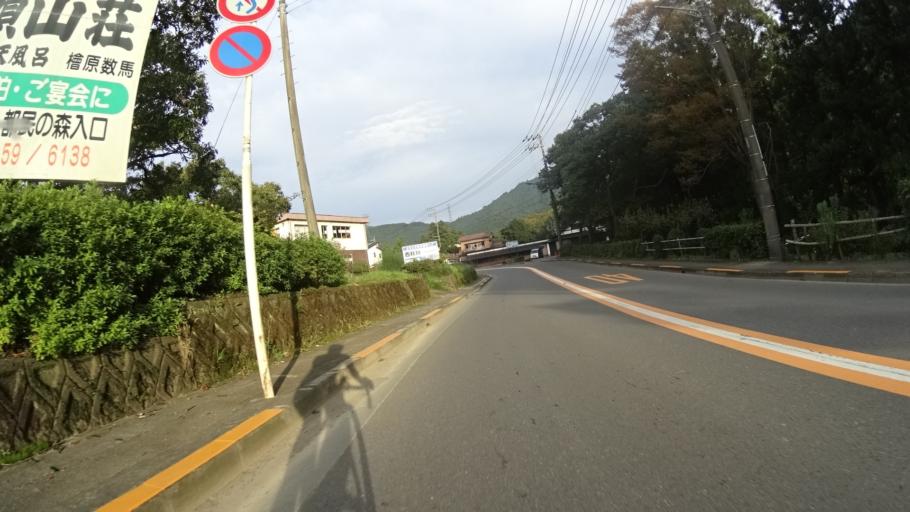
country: JP
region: Tokyo
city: Itsukaichi
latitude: 35.7272
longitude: 139.2066
